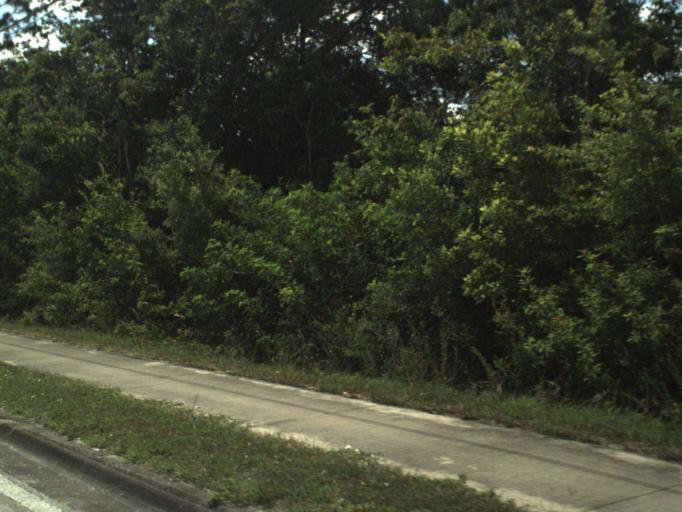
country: US
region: Florida
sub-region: Brevard County
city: June Park
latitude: 28.1280
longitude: -80.6823
